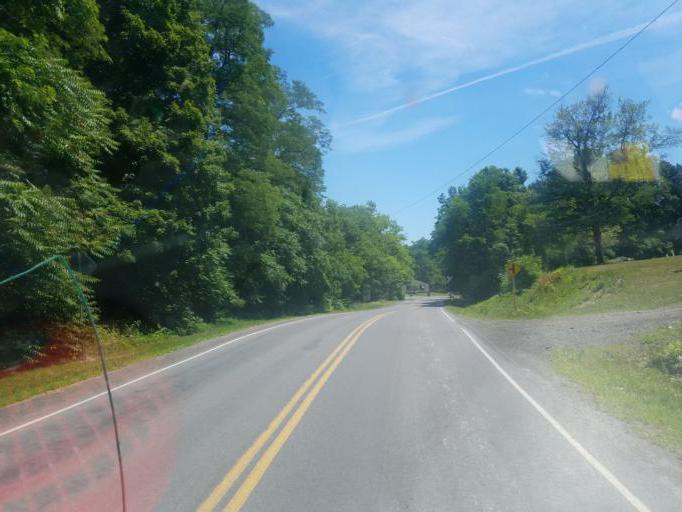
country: US
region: New York
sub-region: Yates County
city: Dundee
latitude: 42.5922
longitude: -76.9561
